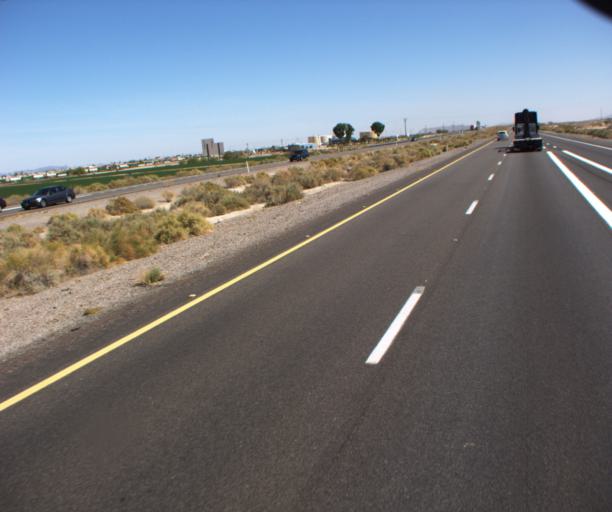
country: US
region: Arizona
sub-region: Yuma County
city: Wellton
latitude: 32.6628
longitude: -114.1377
